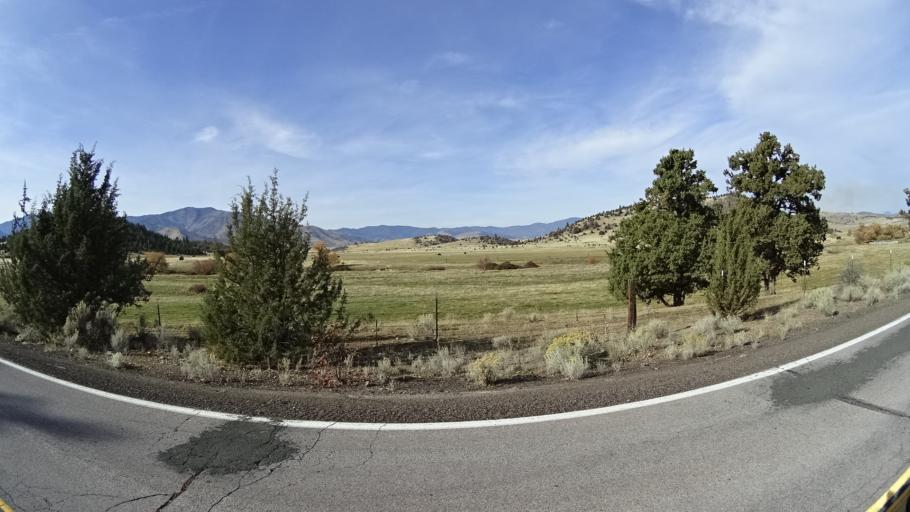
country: US
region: California
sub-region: Siskiyou County
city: Weed
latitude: 41.4740
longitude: -122.4131
